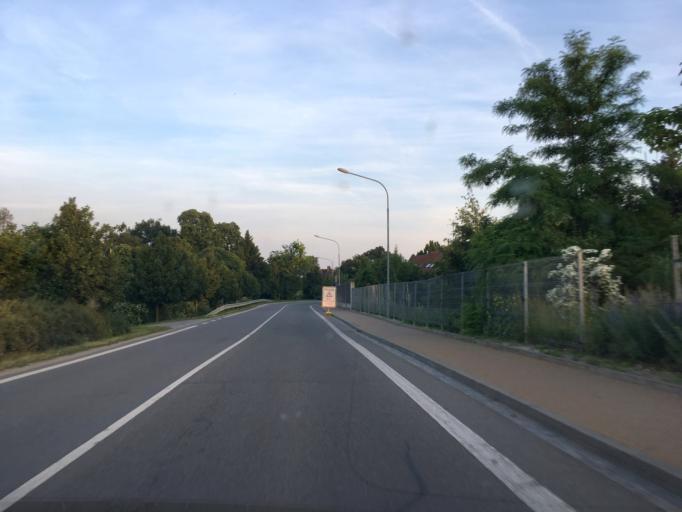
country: CZ
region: South Moravian
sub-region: Okres Breclav
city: Lednice
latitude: 48.7973
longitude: 16.7997
